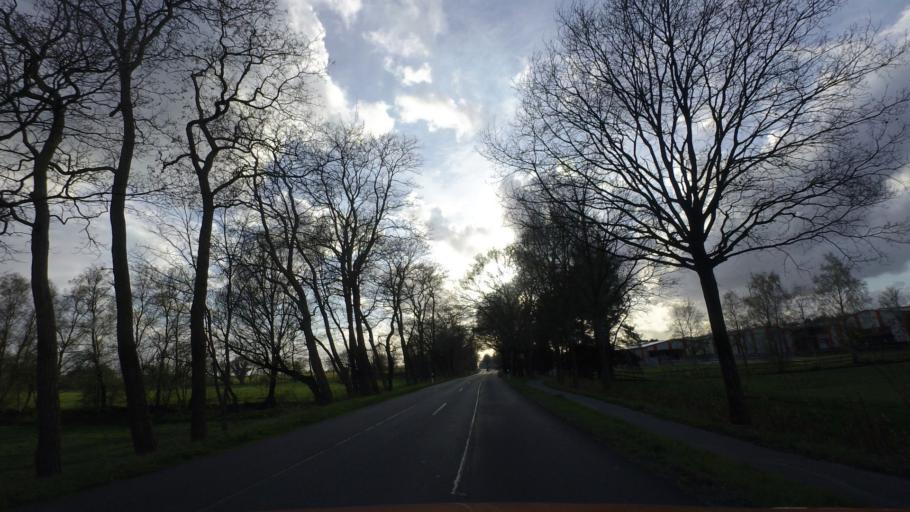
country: DE
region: Lower Saxony
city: Edewecht
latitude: 53.1224
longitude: 8.0405
